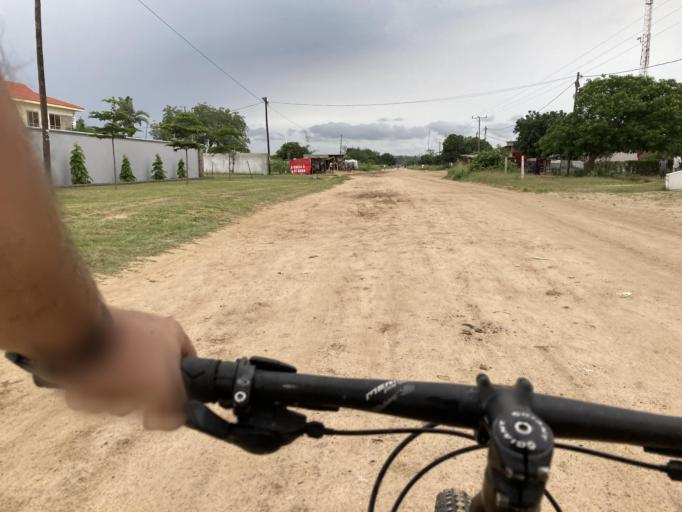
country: MZ
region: Maputo City
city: Maputo
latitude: -26.0419
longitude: 32.5384
